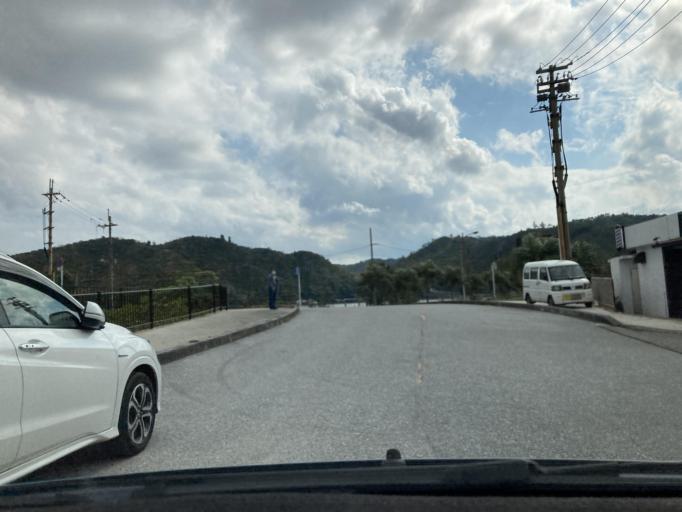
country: JP
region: Okinawa
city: Nago
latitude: 26.6679
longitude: 128.1038
